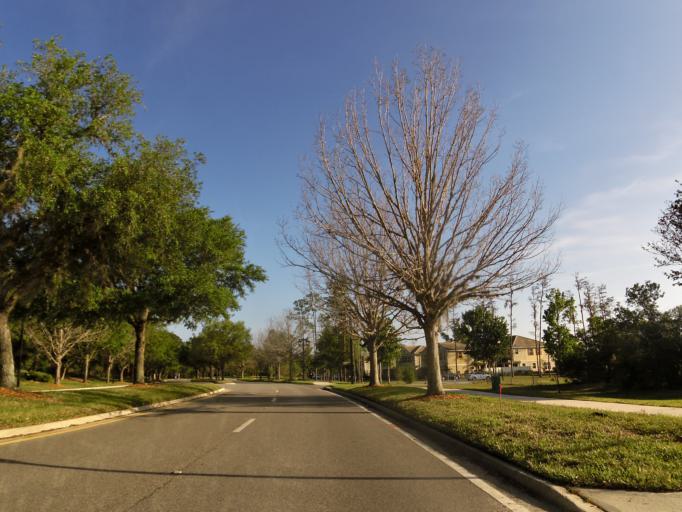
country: US
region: Florida
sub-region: Saint Johns County
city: Villano Beach
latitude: 29.9860
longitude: -81.4773
